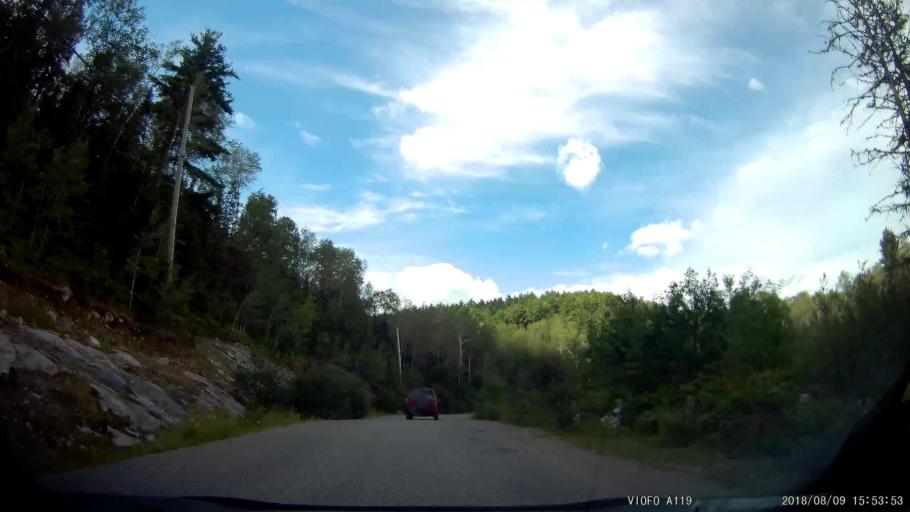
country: CA
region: Ontario
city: Rayside-Balfour
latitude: 46.6074
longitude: -81.5331
